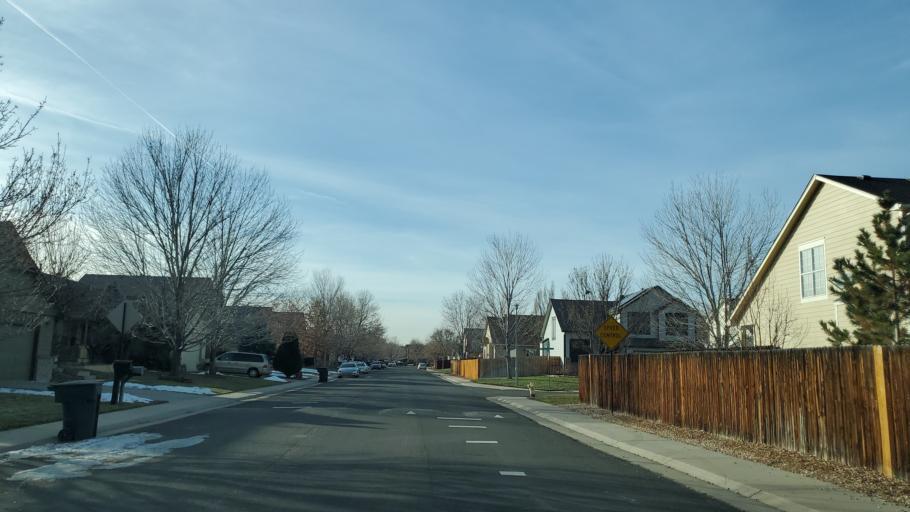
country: US
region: Colorado
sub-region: Adams County
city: Northglenn
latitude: 39.9053
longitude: -104.9551
